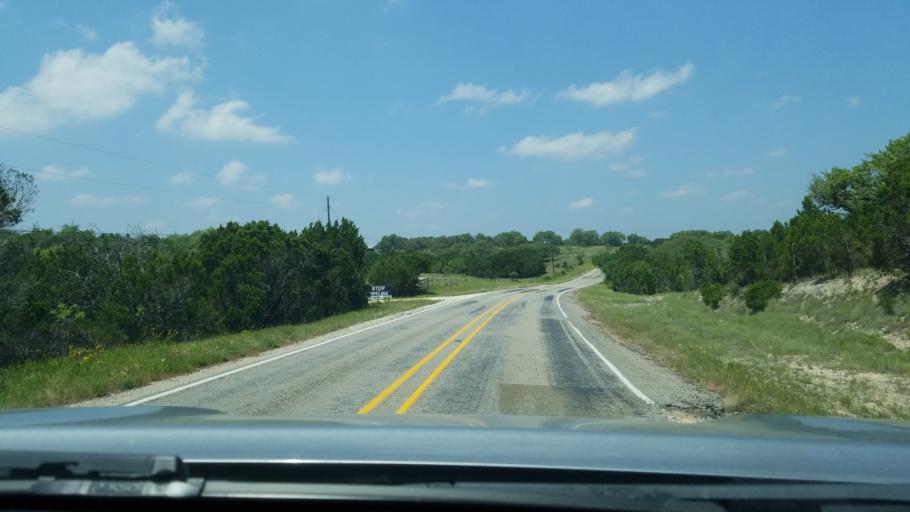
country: US
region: Texas
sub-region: Hays County
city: Woodcreek
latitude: 30.0829
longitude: -98.2273
